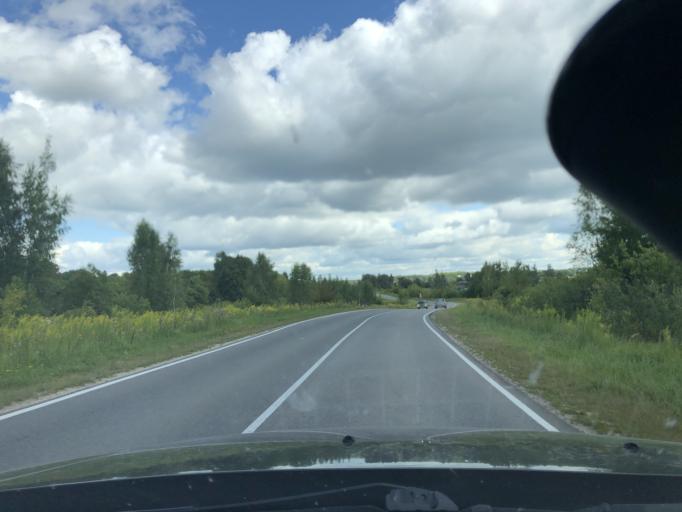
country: RU
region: Tula
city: Yasnogorsk
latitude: 54.4435
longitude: 37.7041
